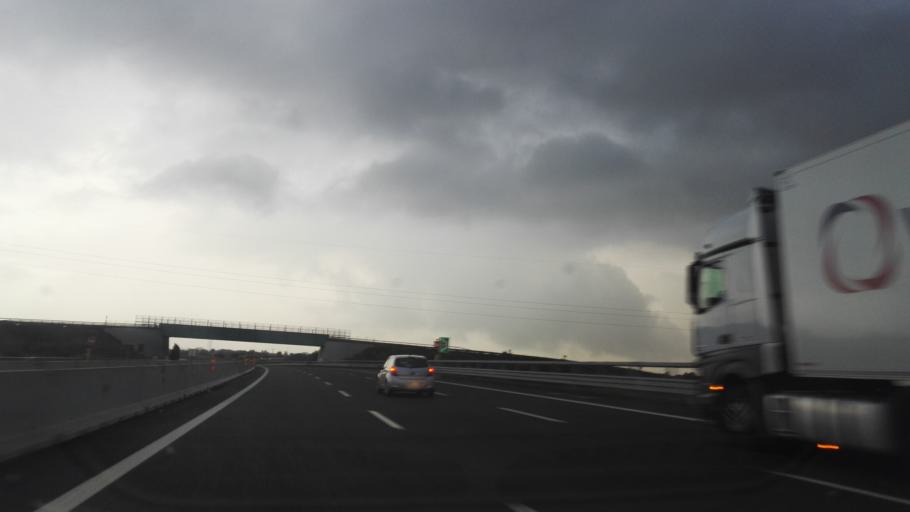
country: IT
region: Lombardy
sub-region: Citta metropolitana di Milano
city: Bellinzago Lombardo
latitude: 45.5317
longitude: 9.4391
